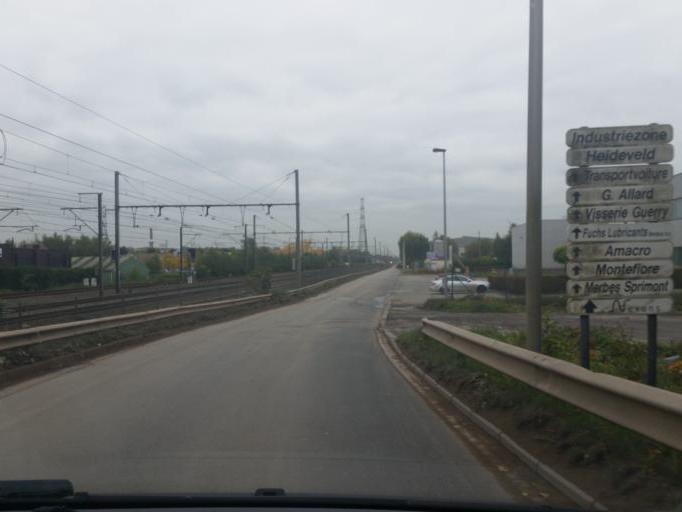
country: BE
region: Flanders
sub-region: Provincie Vlaams-Brabant
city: Beersel
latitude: 50.7632
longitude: 4.2703
